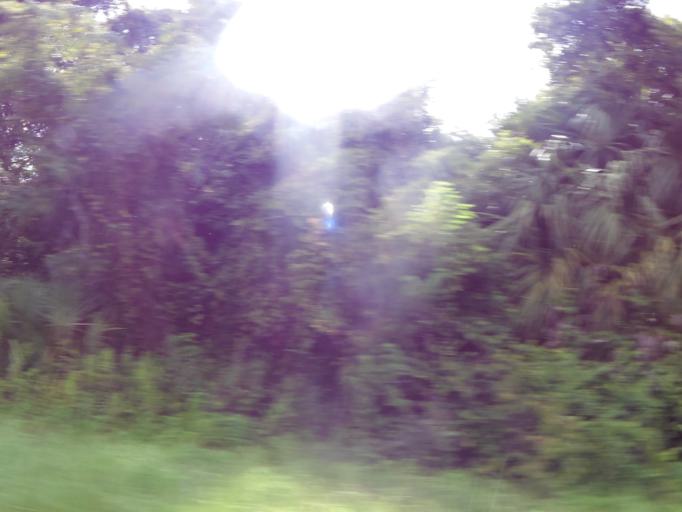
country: US
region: Florida
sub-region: Clay County
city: Green Cove Springs
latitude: 29.9764
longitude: -81.6930
